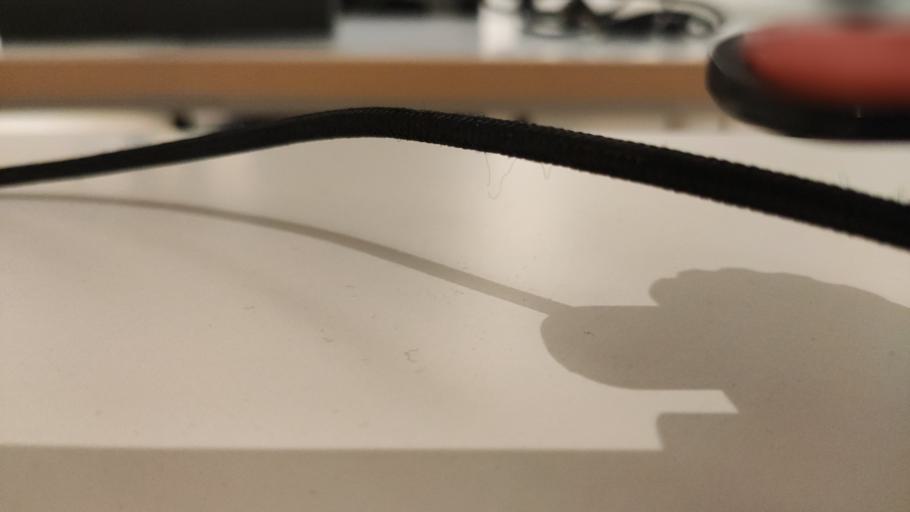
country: RU
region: Moskovskaya
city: Dorokhovo
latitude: 55.5112
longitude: 36.3468
